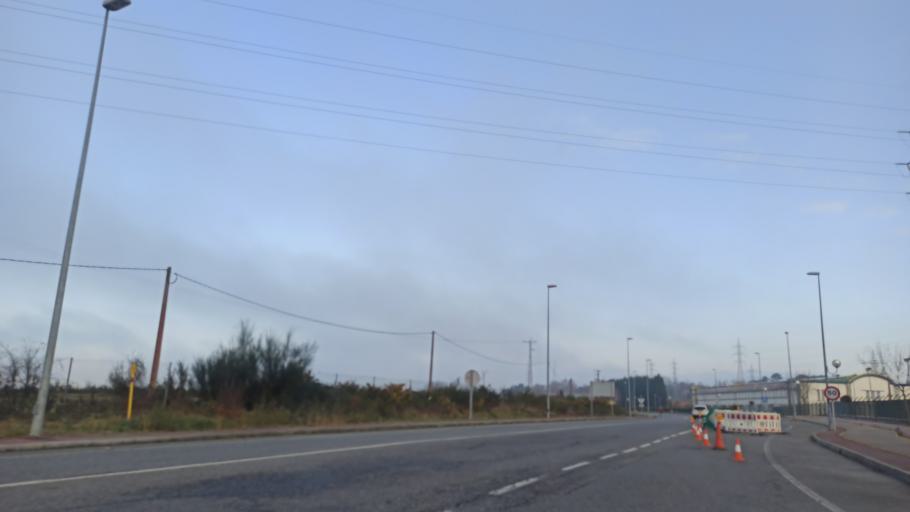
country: ES
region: Galicia
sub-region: Provincia da Coruna
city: As Pontes de Garcia Rodriguez
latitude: 43.4429
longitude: -7.8669
